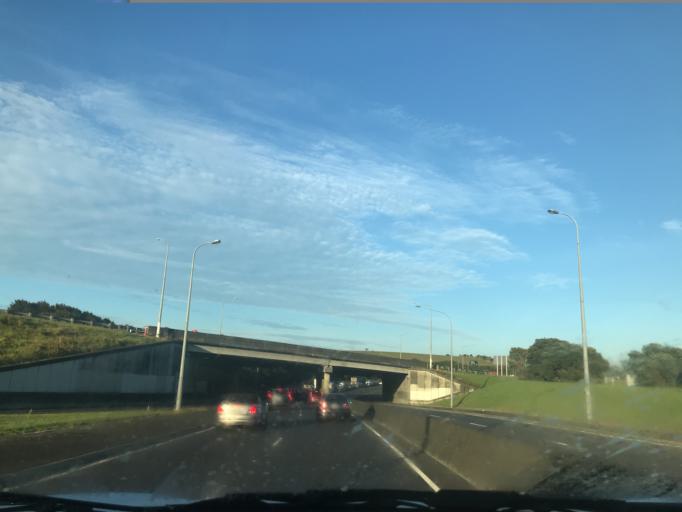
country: NZ
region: Auckland
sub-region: Auckland
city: Tamaki
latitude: -36.9163
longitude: 174.8352
